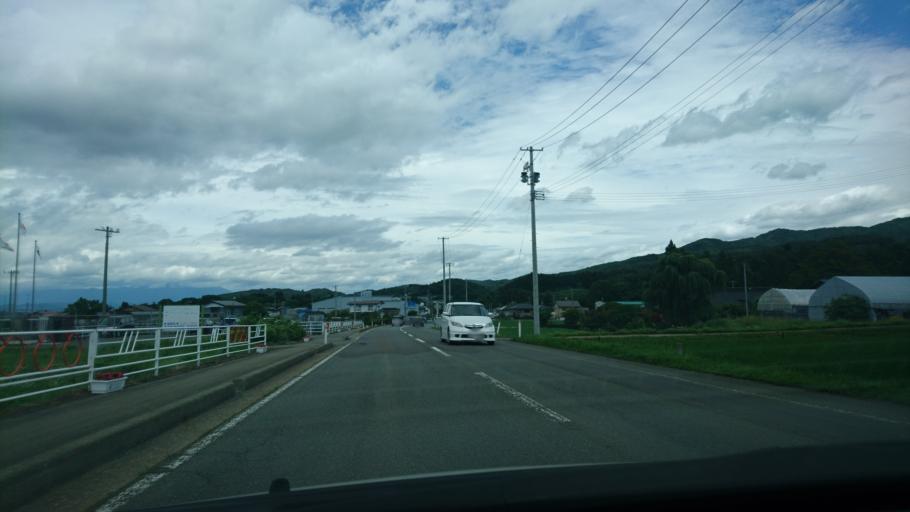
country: JP
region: Iwate
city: Morioka-shi
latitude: 39.6051
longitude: 141.2042
